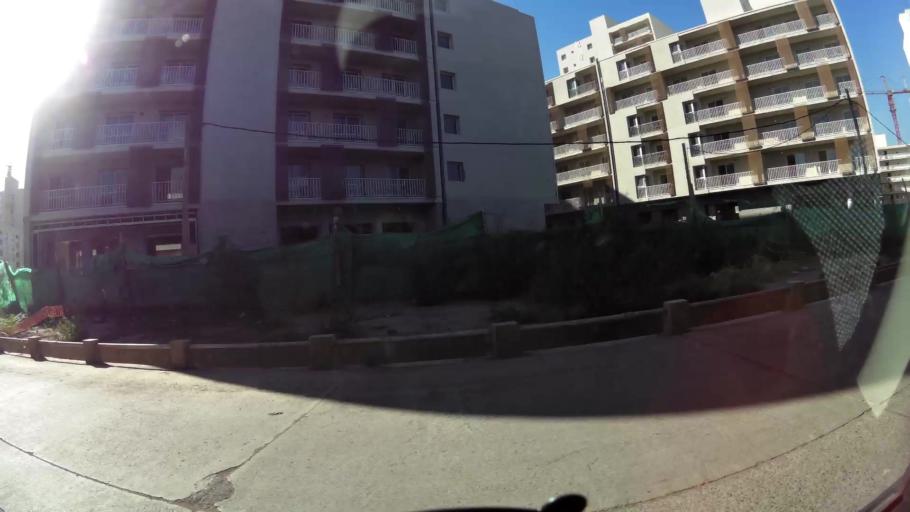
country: AR
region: Mendoza
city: Mendoza
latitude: -32.8767
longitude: -68.8489
